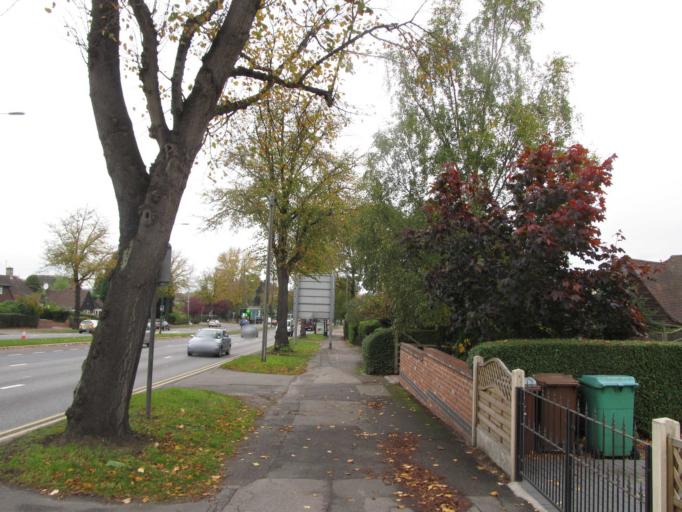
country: GB
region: England
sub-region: Nottingham
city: Nottingham
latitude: 52.9484
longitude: -1.1904
